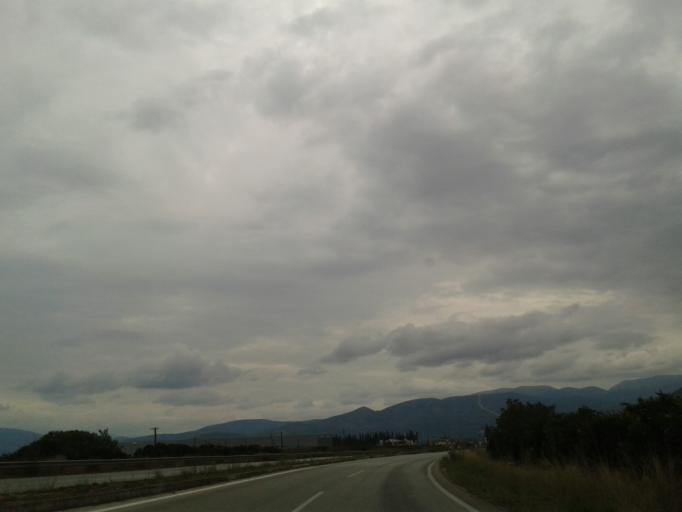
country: GR
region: Peloponnese
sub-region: Nomos Argolidos
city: Argos
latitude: 37.6190
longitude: 22.7336
